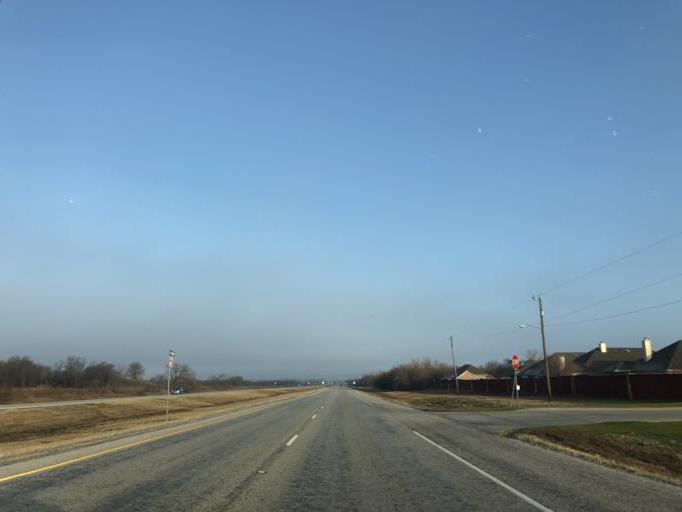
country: US
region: Texas
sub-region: Dallas County
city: Cedar Hill
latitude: 32.6484
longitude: -96.9758
